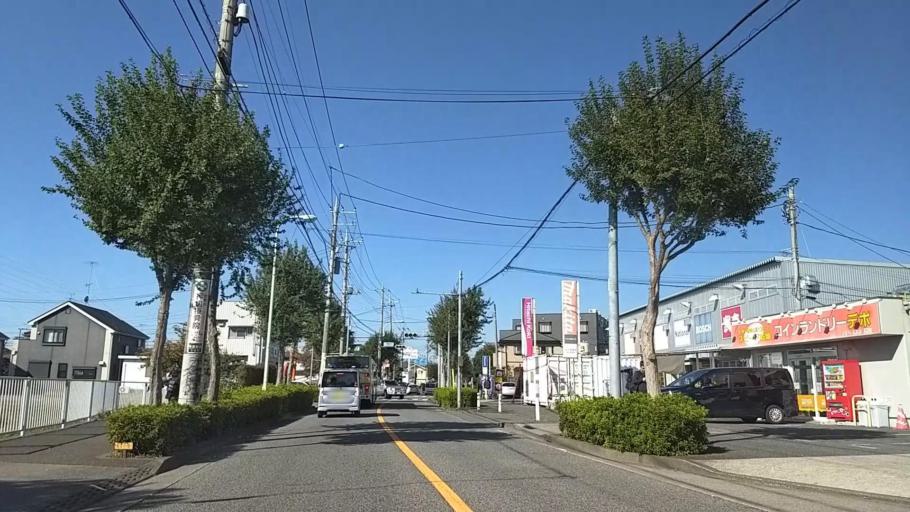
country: JP
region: Tokyo
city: Hino
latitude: 35.5920
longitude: 139.3808
